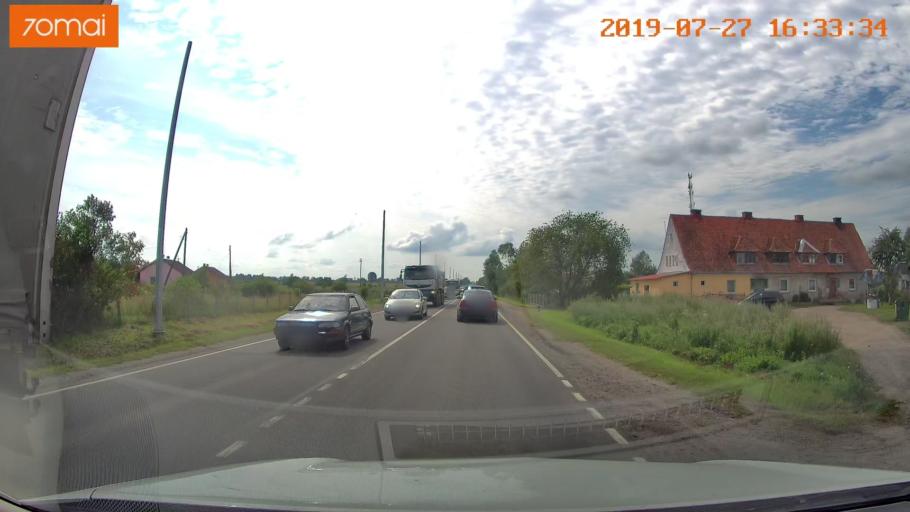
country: RU
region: Kaliningrad
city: Gvardeysk
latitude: 54.6506
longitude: 21.3371
